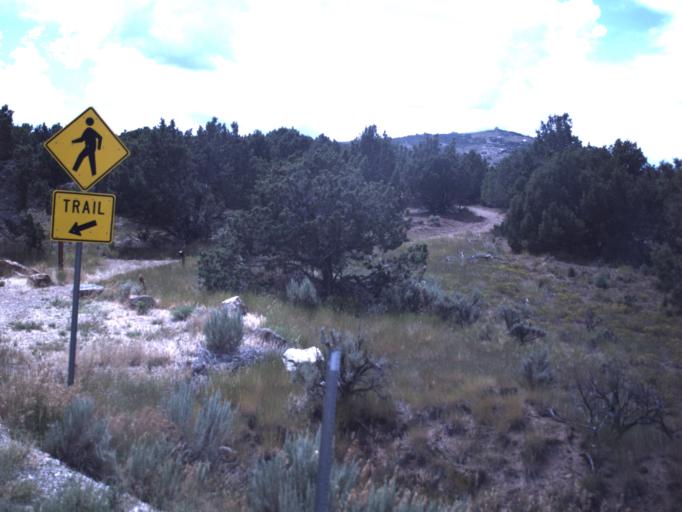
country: US
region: Utah
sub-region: Summit County
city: Oakley
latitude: 40.7724
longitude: -111.3880
